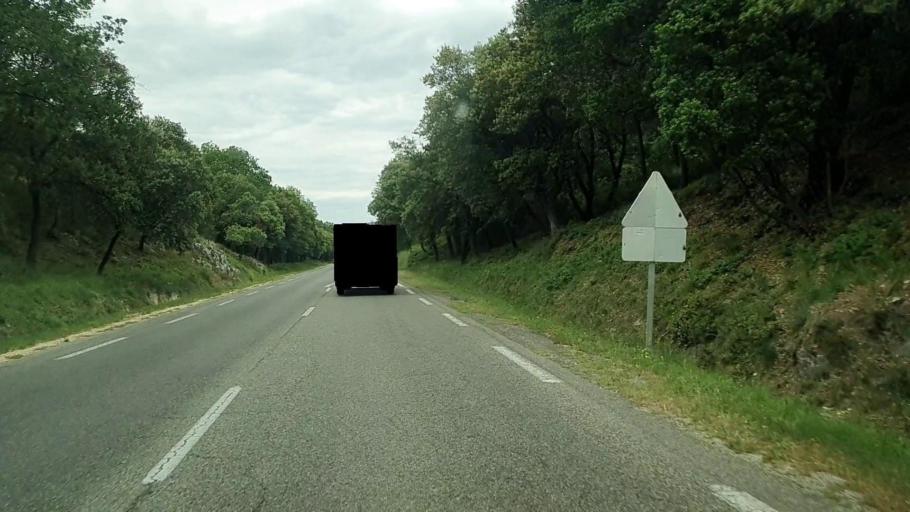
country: FR
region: Languedoc-Roussillon
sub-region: Departement du Gard
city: Connaux
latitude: 44.0682
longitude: 4.5782
